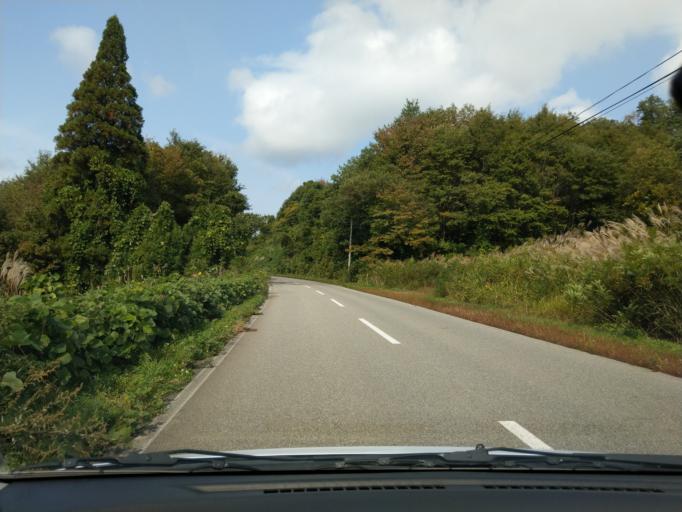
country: JP
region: Akita
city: Omagari
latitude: 39.4931
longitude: 140.3130
